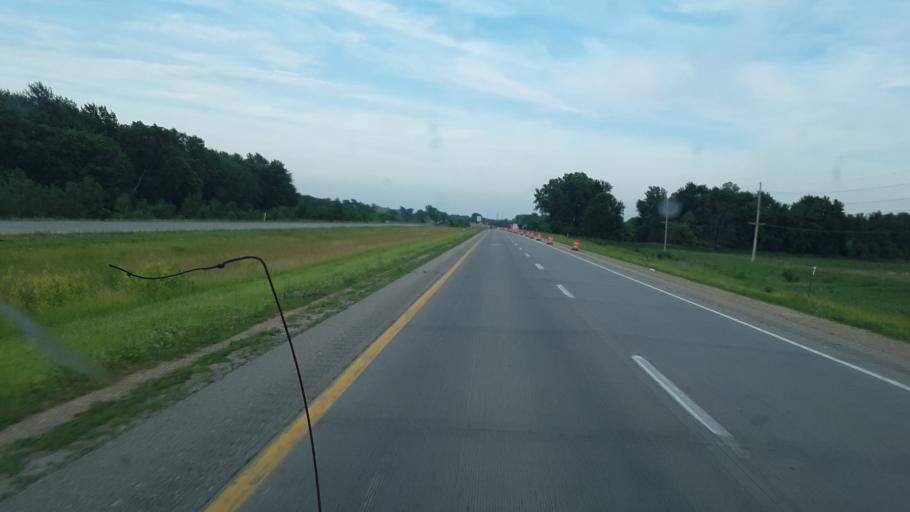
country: US
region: Iowa
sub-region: Tama County
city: Toledo
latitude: 42.0028
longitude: -92.7179
